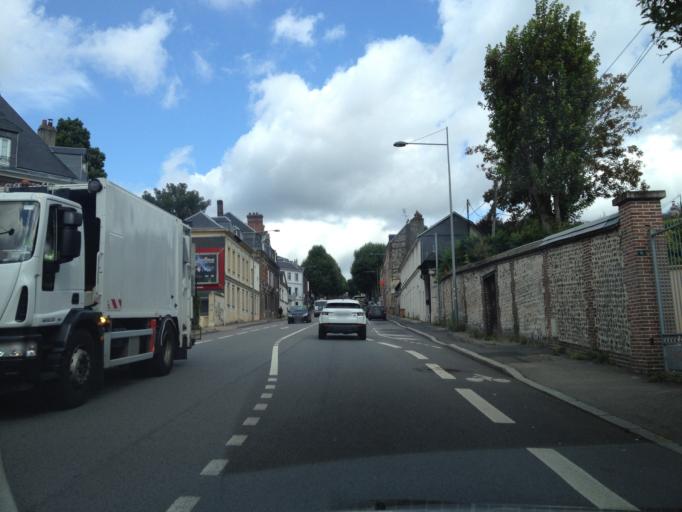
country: FR
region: Haute-Normandie
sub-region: Departement de la Seine-Maritime
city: Rouen
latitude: 49.4494
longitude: 1.0993
